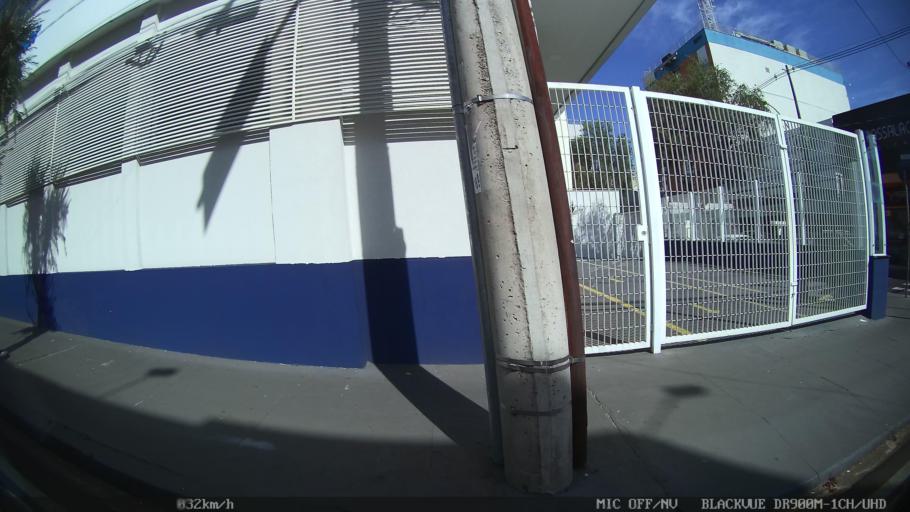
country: BR
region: Sao Paulo
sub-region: Franca
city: Franca
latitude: -20.5358
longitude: -47.4008
